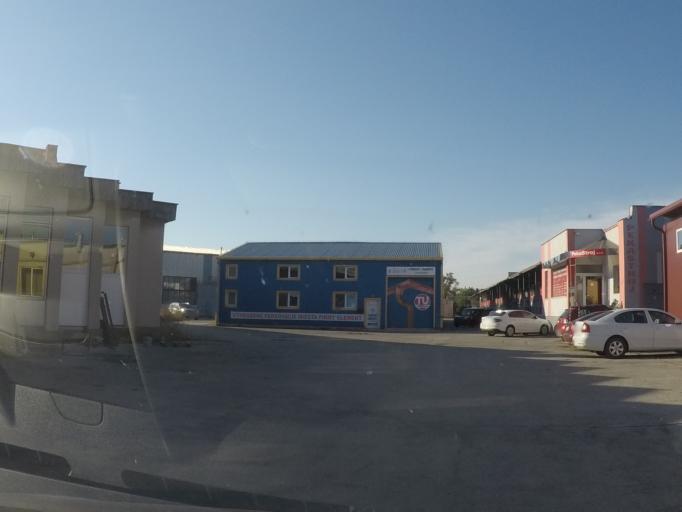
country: SK
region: Nitriansky
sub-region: Okres Nitra
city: Nitra
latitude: 48.2889
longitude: 18.0911
